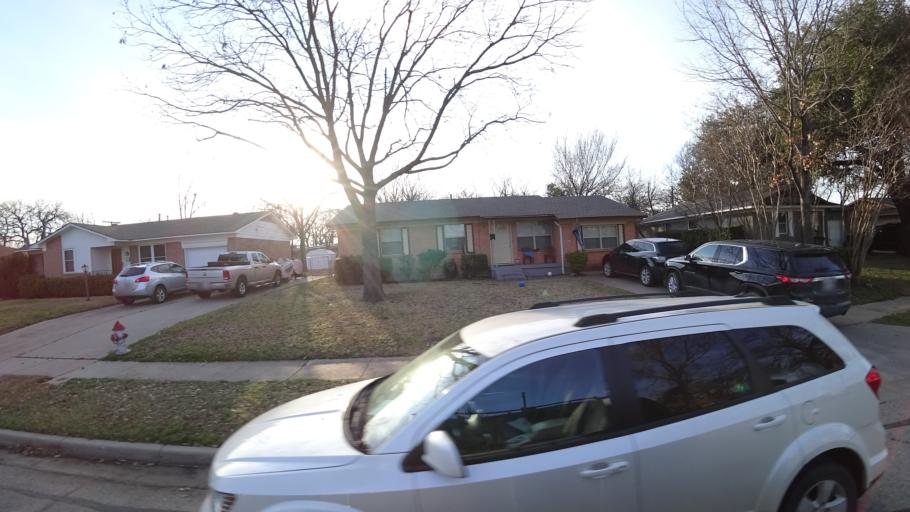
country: US
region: Texas
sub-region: Denton County
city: Lewisville
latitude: 33.0377
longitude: -96.9993
